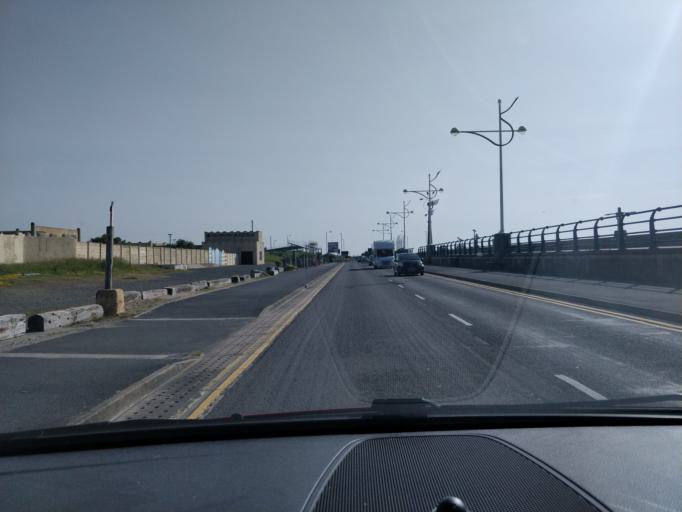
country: GB
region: England
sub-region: Sefton
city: Southport
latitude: 53.6499
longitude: -3.0195
